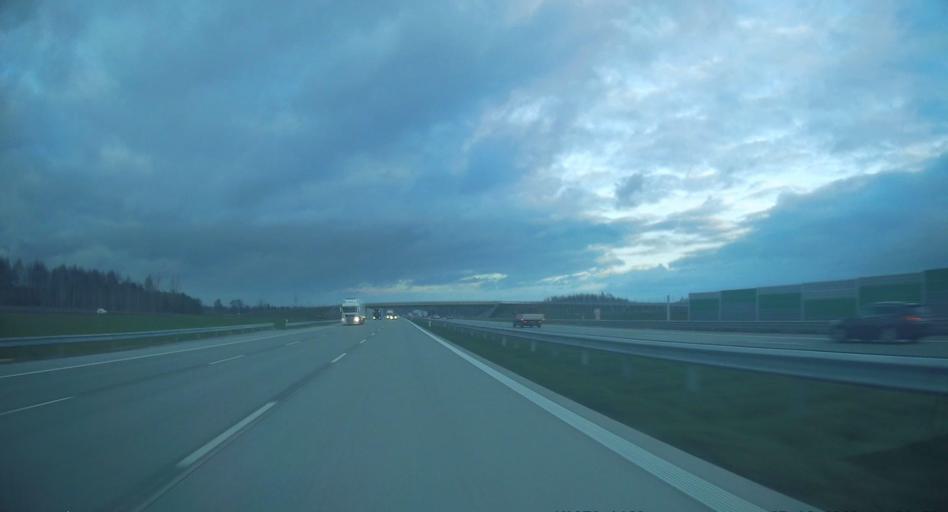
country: PL
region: Lodz Voivodeship
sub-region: Powiat piotrkowski
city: Wola Krzysztoporska
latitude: 51.3064
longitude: 19.5617
